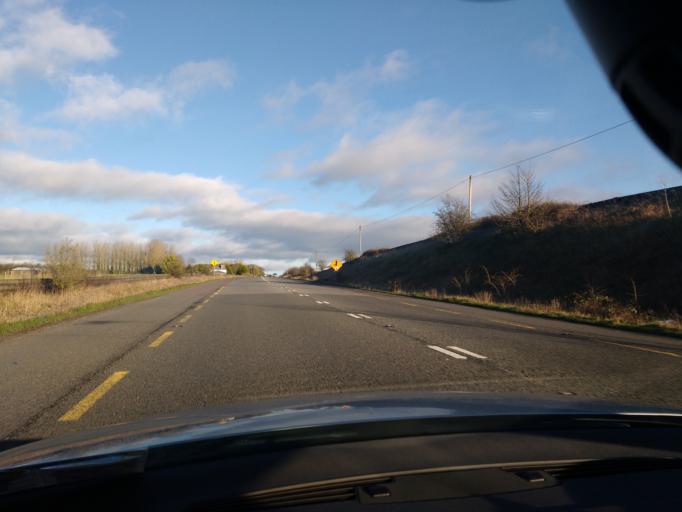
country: IE
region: Leinster
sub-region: Laois
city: Rathdowney
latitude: 52.6993
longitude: -7.6245
